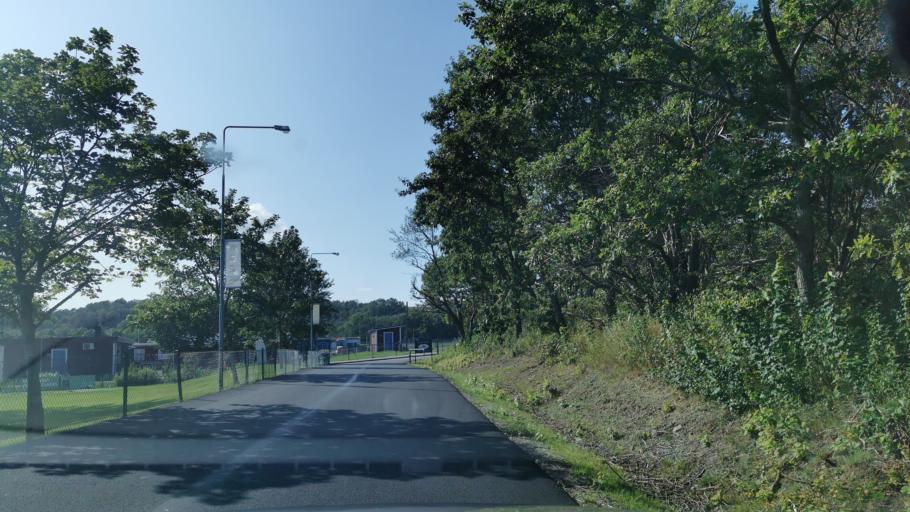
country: SE
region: Vaestra Goetaland
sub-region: Goteborg
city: Majorna
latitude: 57.6412
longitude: 11.9220
